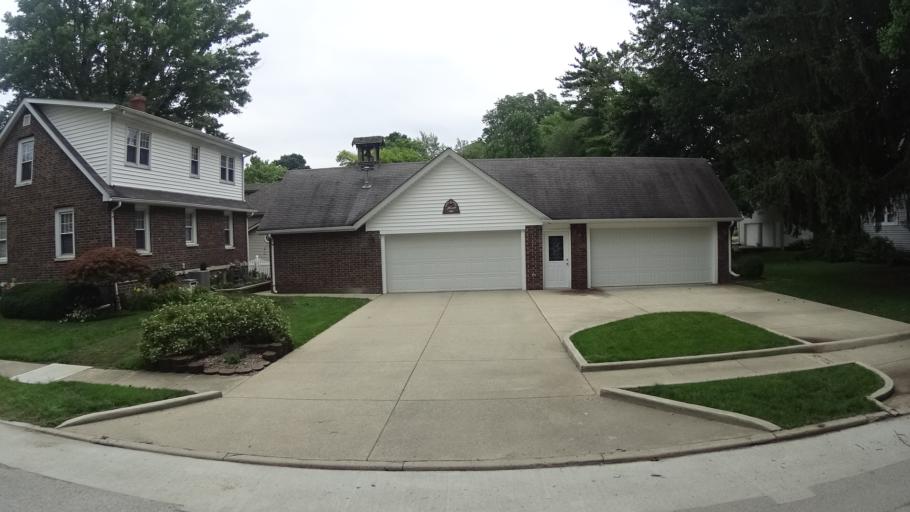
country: US
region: Indiana
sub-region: Madison County
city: Pendleton
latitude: 40.0021
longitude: -85.7518
